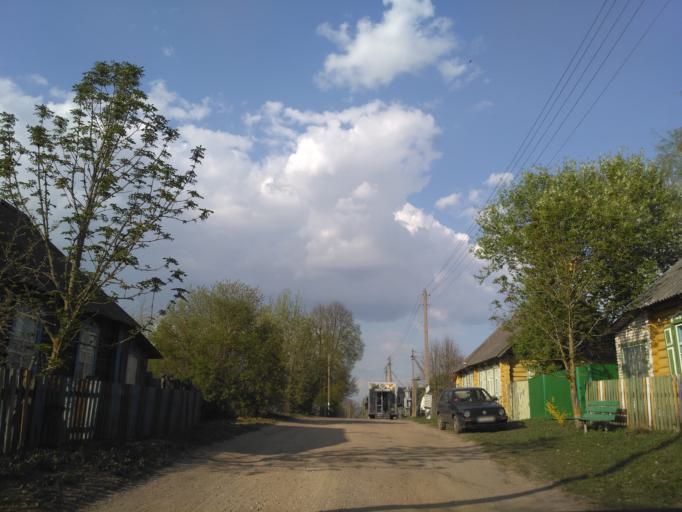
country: BY
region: Minsk
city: Khalopyenichy
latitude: 54.5018
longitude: 28.8467
